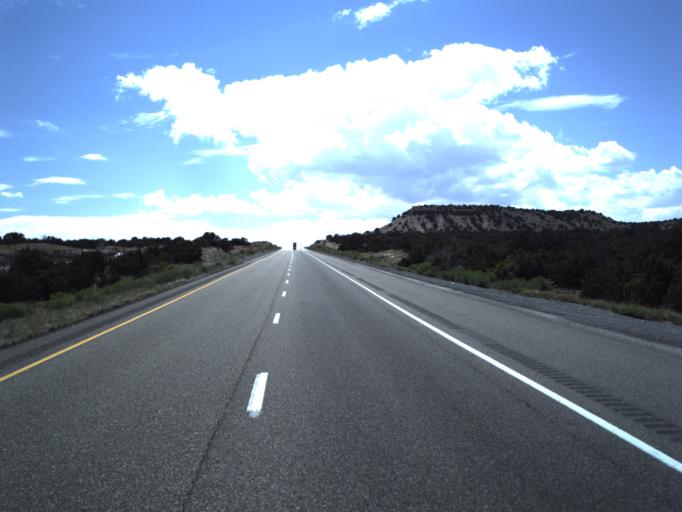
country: US
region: Utah
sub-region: Emery County
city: Castle Dale
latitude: 38.9128
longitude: -110.5228
